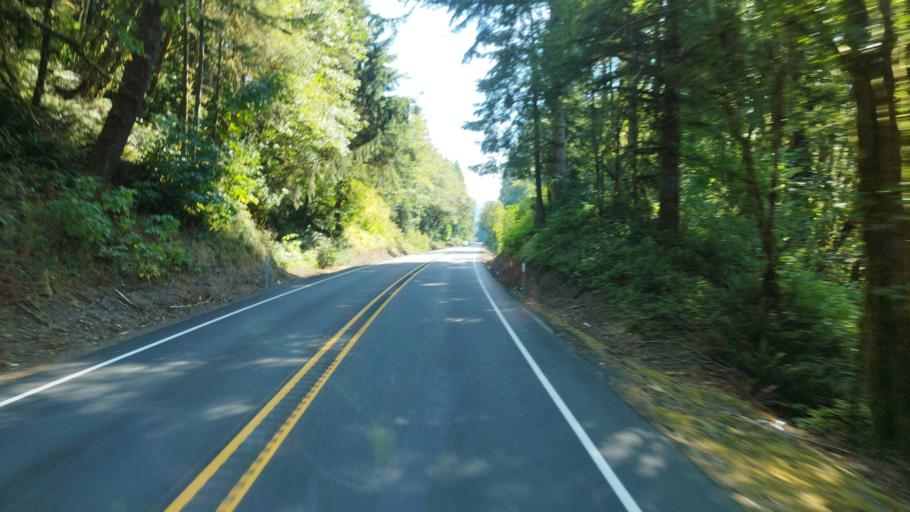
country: US
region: Oregon
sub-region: Clatsop County
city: Seaside
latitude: 45.8806
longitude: -123.6043
